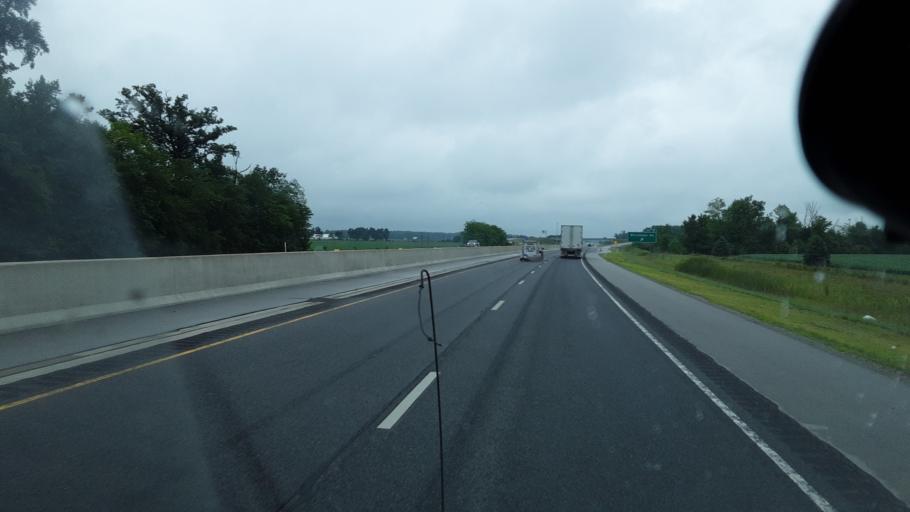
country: US
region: Indiana
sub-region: Wells County
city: Ossian
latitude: 40.9718
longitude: -85.1166
